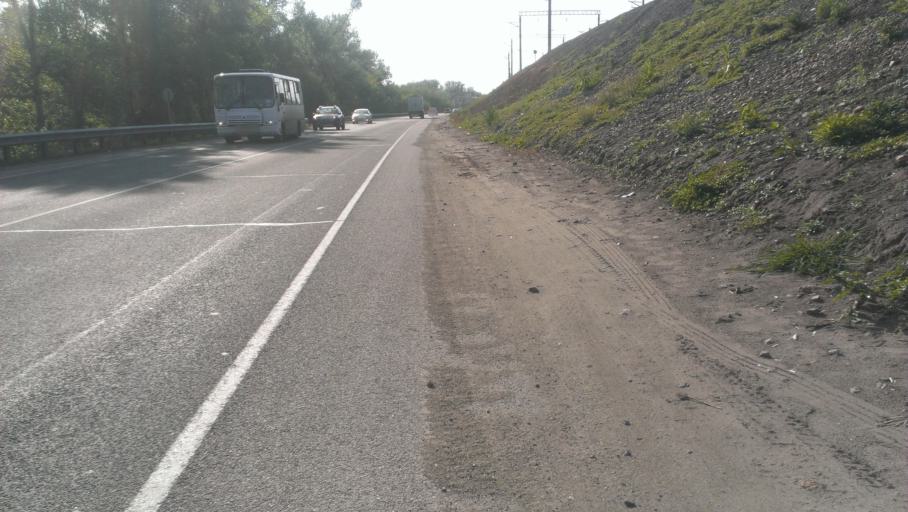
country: RU
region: Altai Krai
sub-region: Gorod Barnaulskiy
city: Barnaul
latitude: 53.3675
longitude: 83.8355
